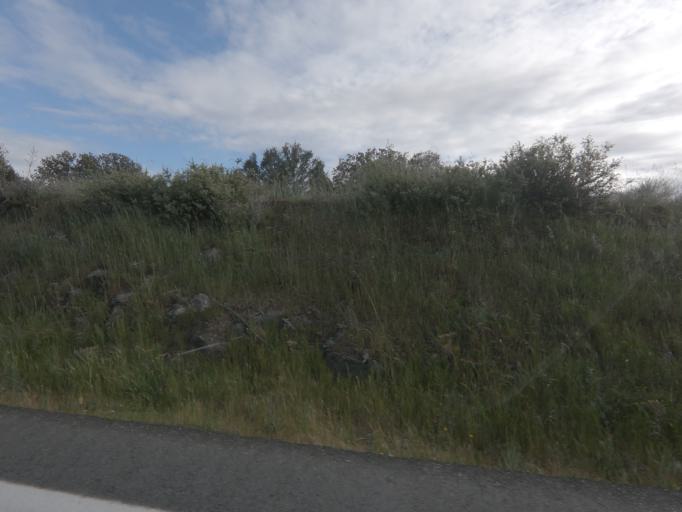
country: ES
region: Extremadura
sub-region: Provincia de Caceres
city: Huelaga
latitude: 40.0344
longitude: -6.6227
